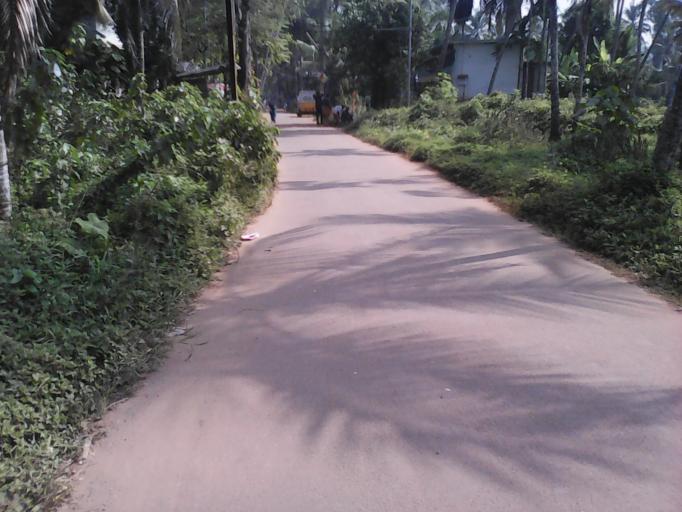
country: IN
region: Kerala
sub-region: Kozhikode
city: Kozhikode
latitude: 11.2801
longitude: 75.8156
